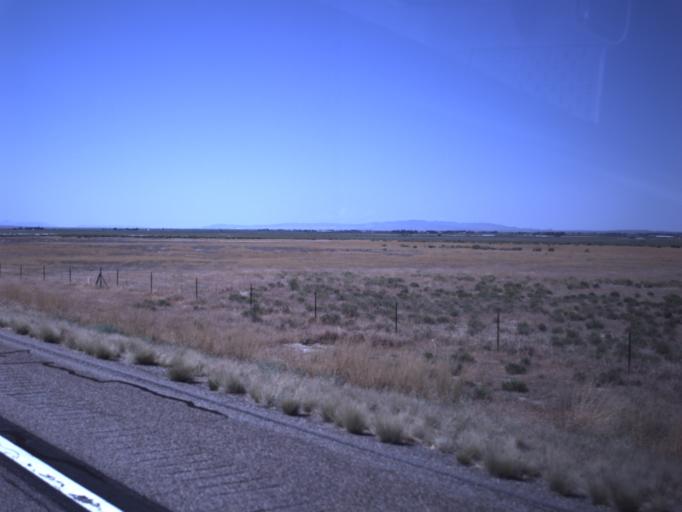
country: US
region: Utah
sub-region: Millard County
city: Delta
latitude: 39.3604
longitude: -112.4965
